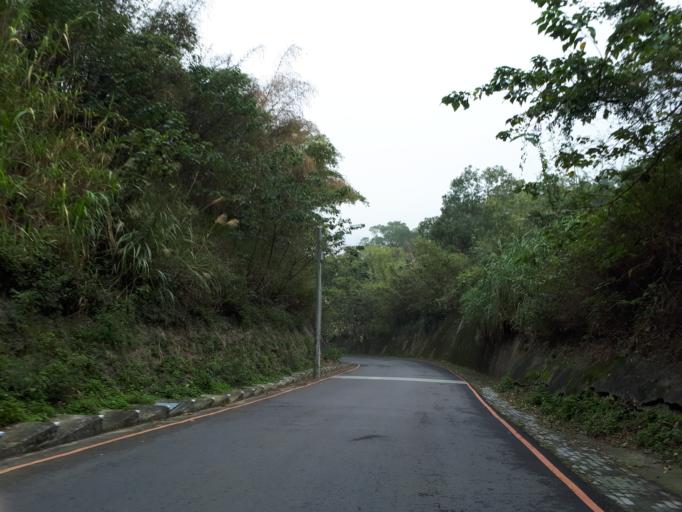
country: TW
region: Taiwan
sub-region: Hsinchu
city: Zhubei
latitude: 24.7391
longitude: 121.0835
